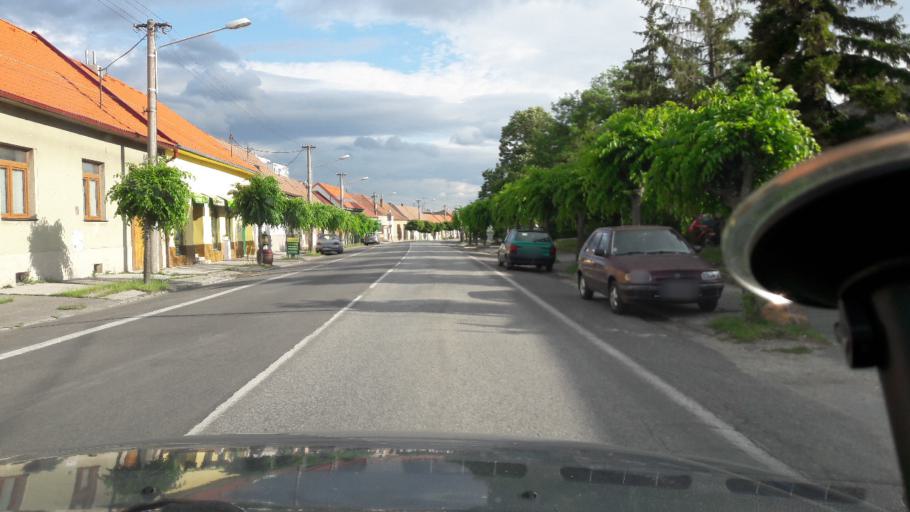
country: SK
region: Bratislavsky
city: Modra
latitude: 48.3328
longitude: 17.3051
